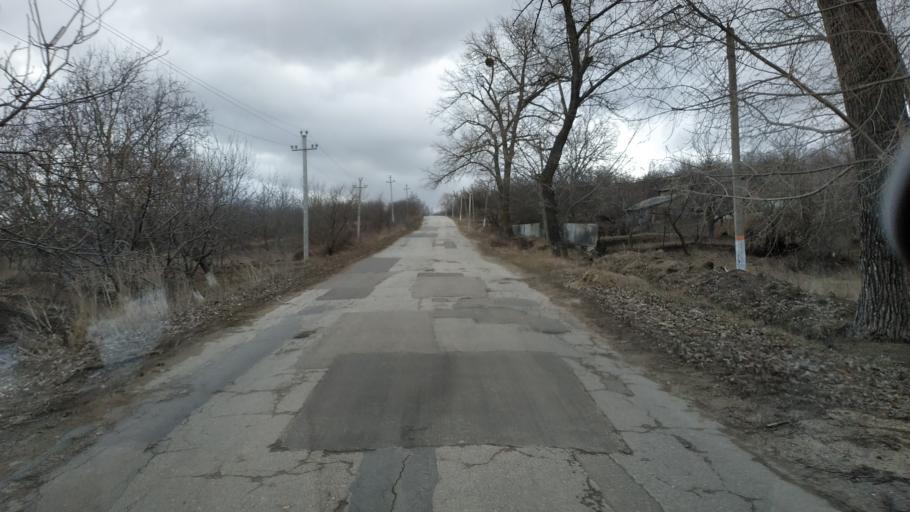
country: MD
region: Stinga Nistrului
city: Bucovat
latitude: 47.2251
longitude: 28.4260
